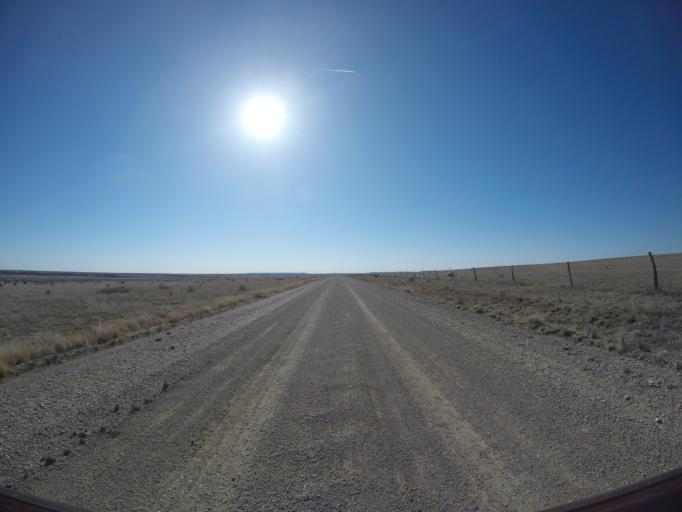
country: US
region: Colorado
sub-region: Otero County
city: La Junta
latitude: 37.7340
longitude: -103.6207
